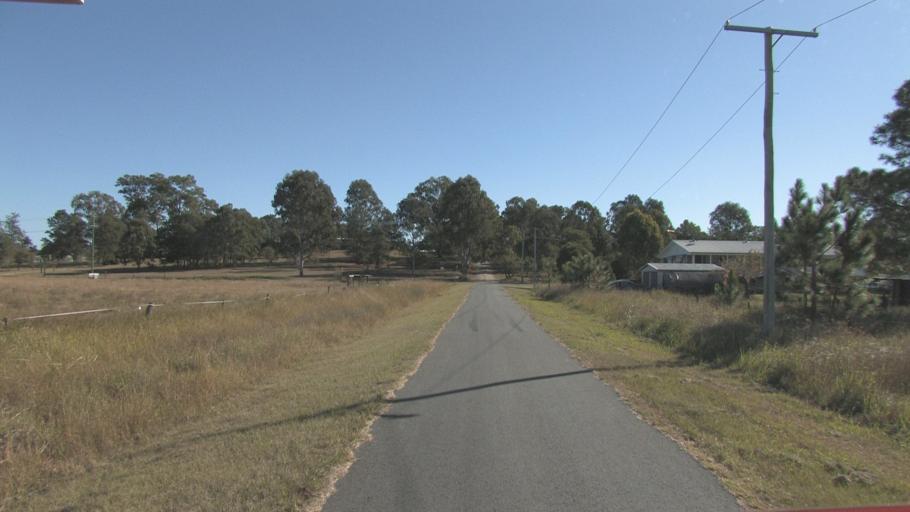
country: AU
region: Queensland
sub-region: Logan
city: North Maclean
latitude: -27.7799
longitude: 153.0203
